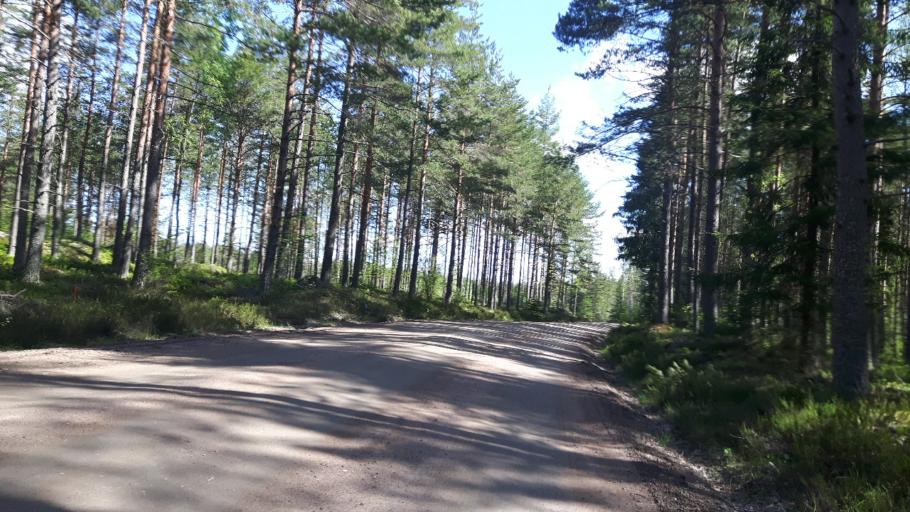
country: FI
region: Kymenlaakso
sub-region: Kotka-Hamina
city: Hamina
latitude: 60.5248
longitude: 27.2805
